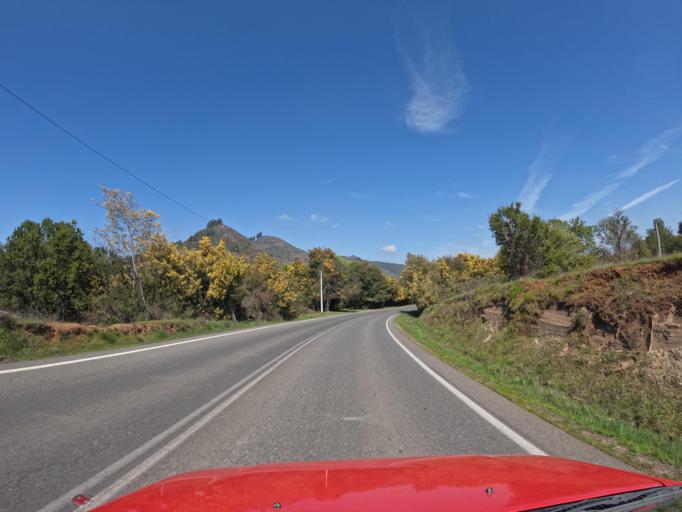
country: CL
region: Maule
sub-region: Provincia de Talca
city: San Clemente
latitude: -35.4801
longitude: -71.2695
